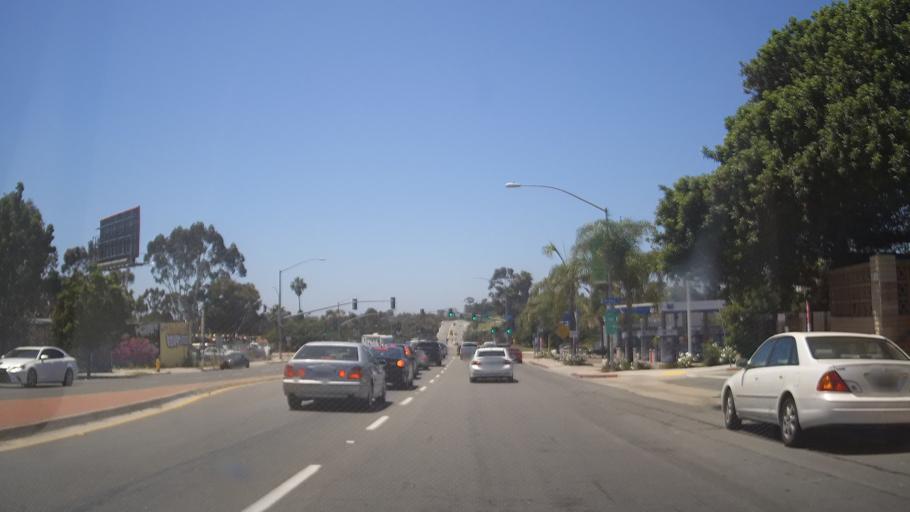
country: US
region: California
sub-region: San Diego County
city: National City
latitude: 32.7043
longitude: -117.0924
